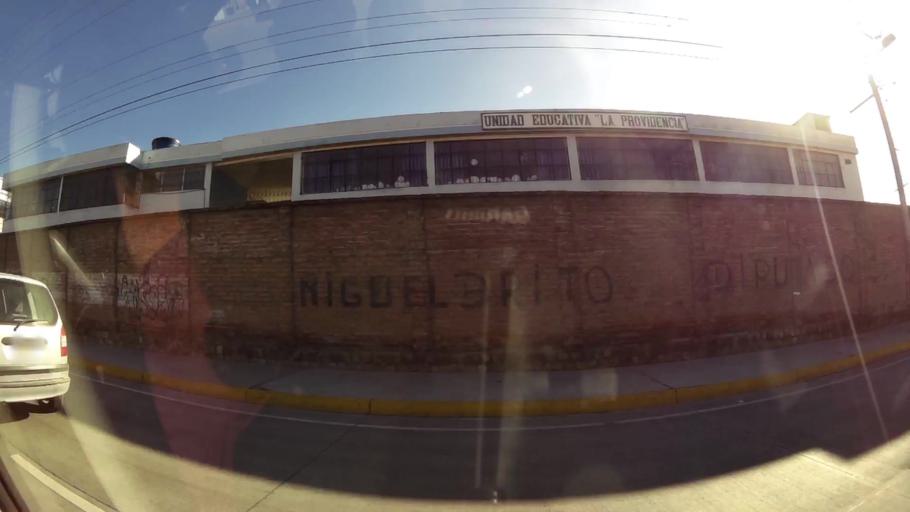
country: EC
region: Chimborazo
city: Riobamba
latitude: -1.6728
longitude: -78.6623
